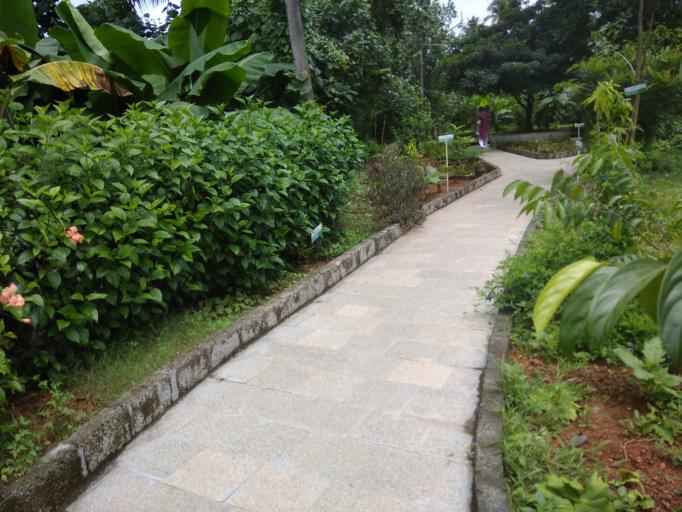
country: IN
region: Kerala
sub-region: Thrissur District
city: Trichur
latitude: 10.4580
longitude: 76.2384
